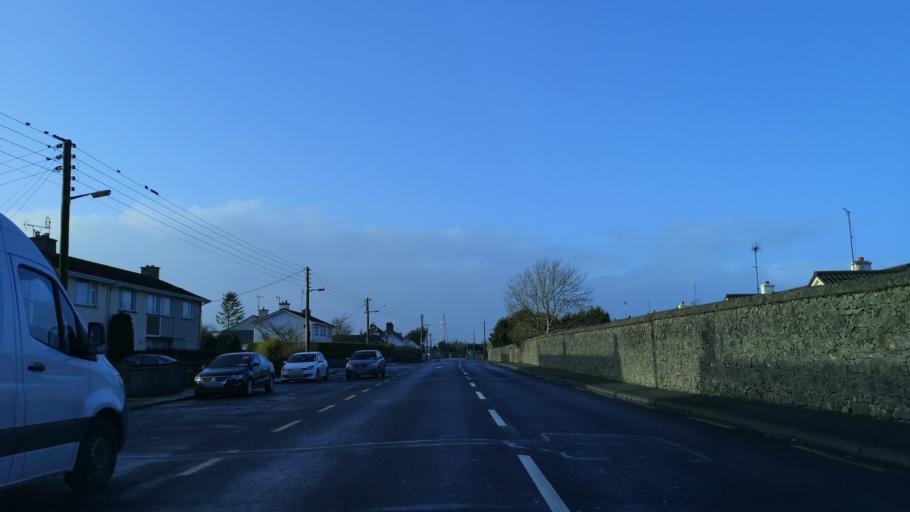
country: IE
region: Connaught
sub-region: County Galway
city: Tuam
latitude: 53.5090
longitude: -8.8414
